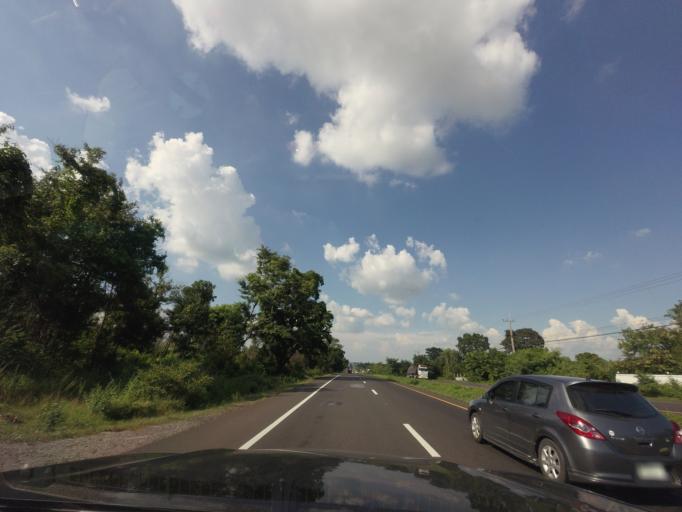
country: TH
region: Nakhon Ratchasima
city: Bua Lai
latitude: 15.6980
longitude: 102.5829
